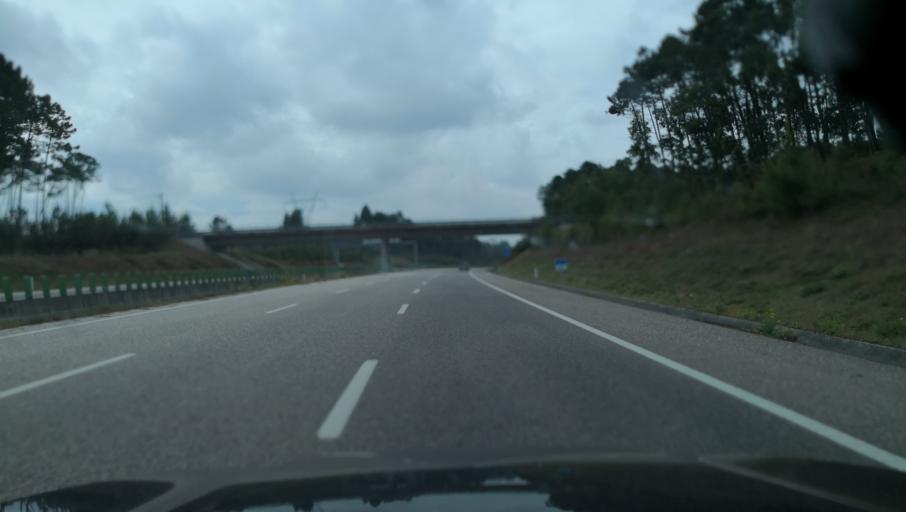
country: PT
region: Leiria
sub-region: Pombal
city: Lourical
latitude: 39.9655
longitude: -8.7776
